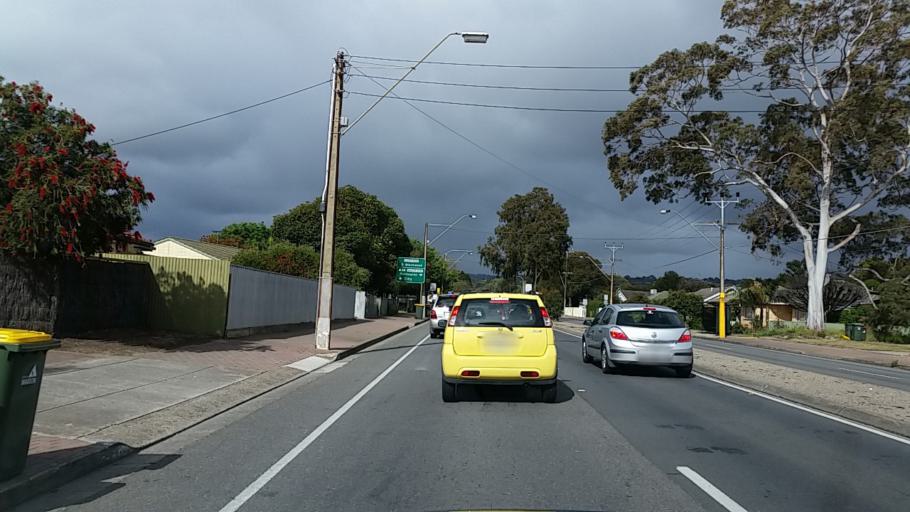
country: AU
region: South Australia
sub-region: Marion
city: Sturt
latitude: -35.0172
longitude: 138.5558
